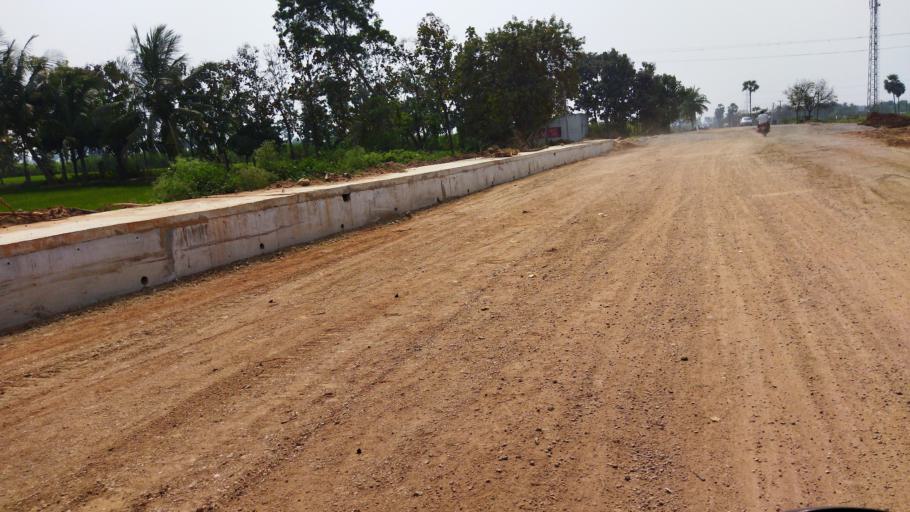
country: IN
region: Telangana
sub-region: Nalgonda
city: Nalgonda
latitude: 17.1216
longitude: 79.3658
